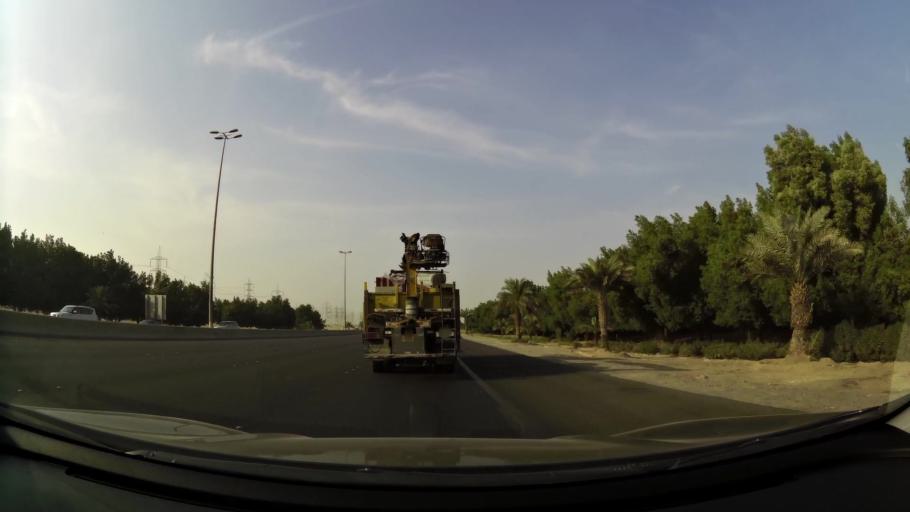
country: KW
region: Mubarak al Kabir
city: Mubarak al Kabir
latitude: 29.1960
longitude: 48.0629
